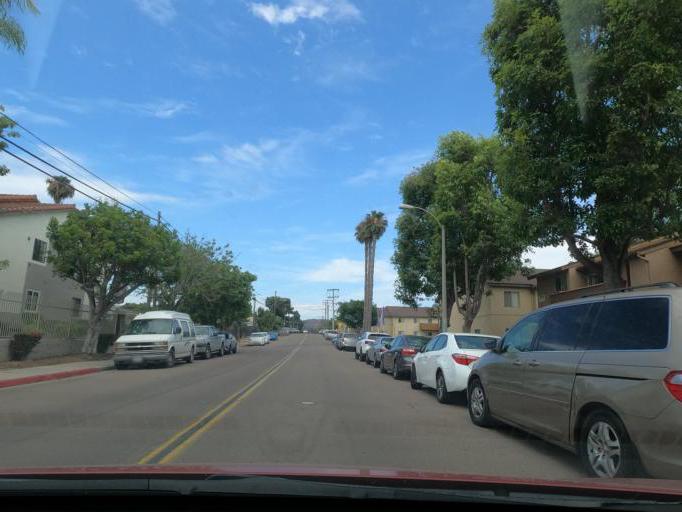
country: US
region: California
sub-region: San Diego County
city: Imperial Beach
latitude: 32.5582
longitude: -117.0566
